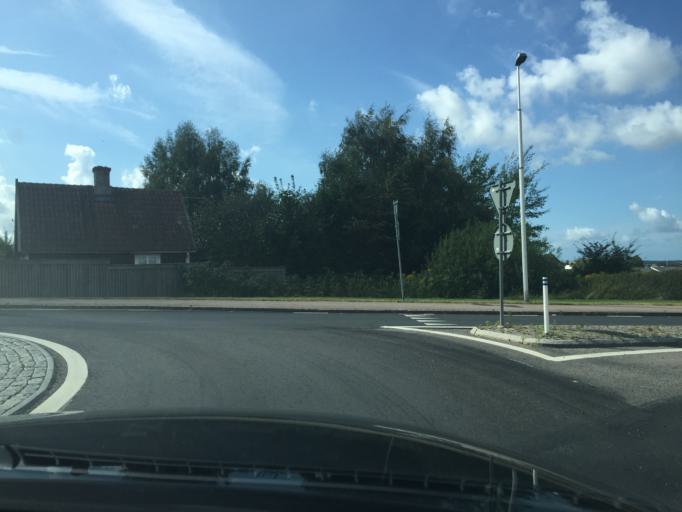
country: SE
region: Halland
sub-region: Laholms Kommun
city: Laholm
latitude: 56.5076
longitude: 13.0366
